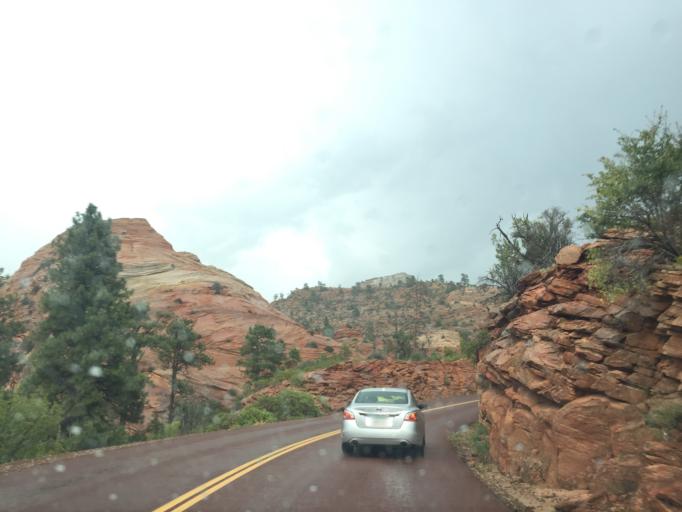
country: US
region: Utah
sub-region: Washington County
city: Hildale
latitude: 37.2213
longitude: -112.9169
